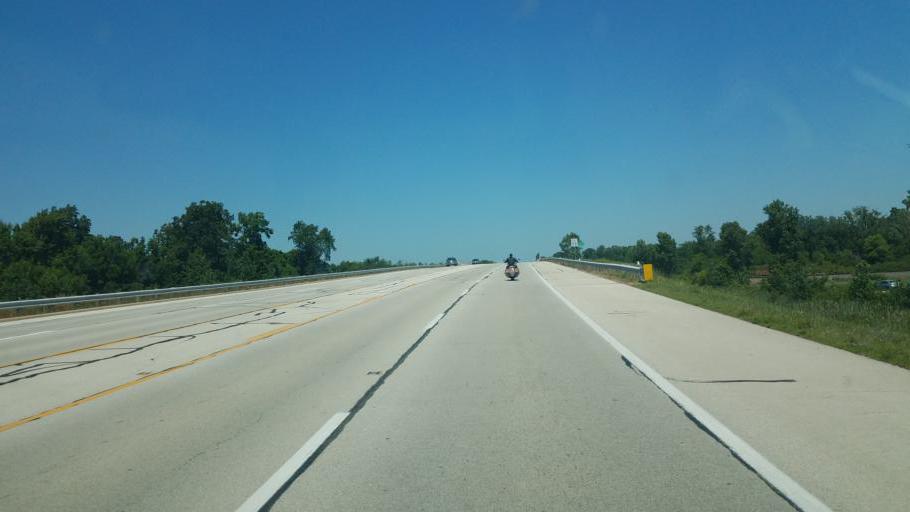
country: US
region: Ohio
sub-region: Sandusky County
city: Fremont
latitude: 41.3816
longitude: -83.1165
